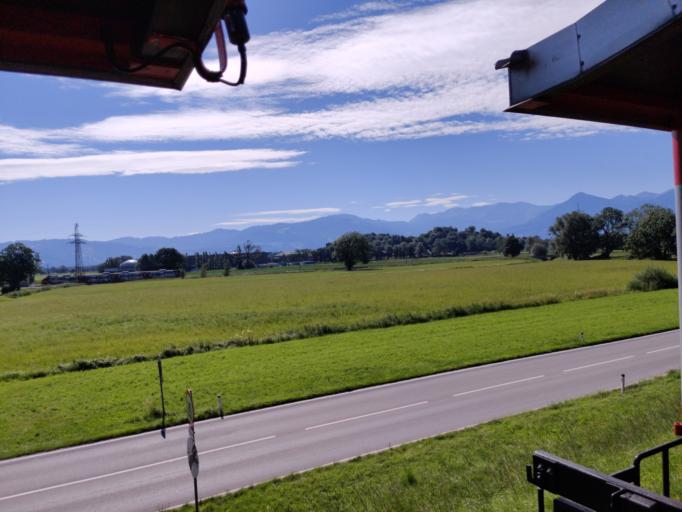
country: AT
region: Vorarlberg
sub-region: Politischer Bezirk Bregenz
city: Fussach
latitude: 47.4651
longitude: 9.6705
